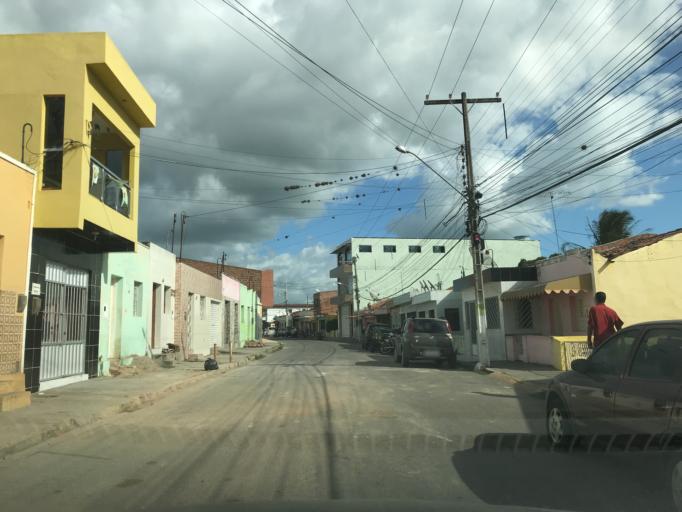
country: BR
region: Pernambuco
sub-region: Bezerros
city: Bezerros
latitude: -8.2412
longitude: -35.7547
